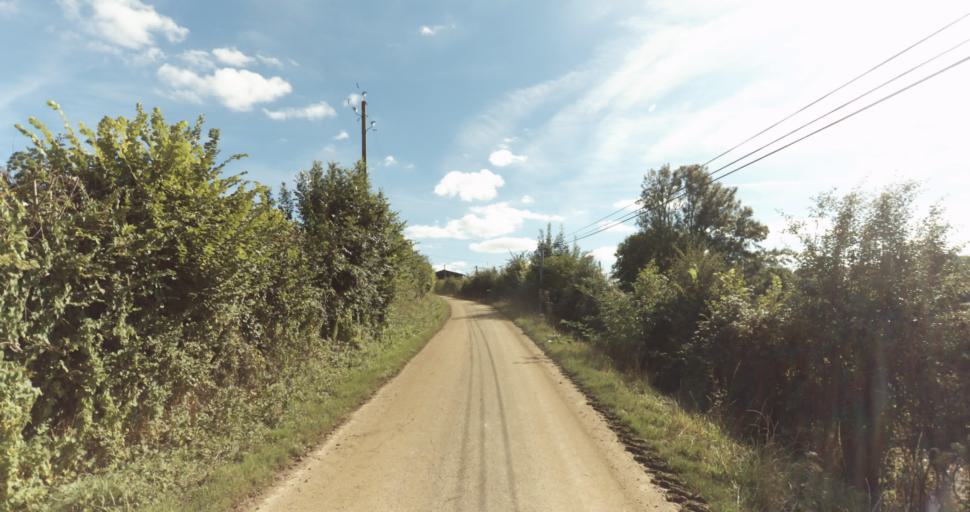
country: FR
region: Lower Normandy
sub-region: Departement de l'Orne
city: Vimoutiers
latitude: 48.9333
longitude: 0.1302
